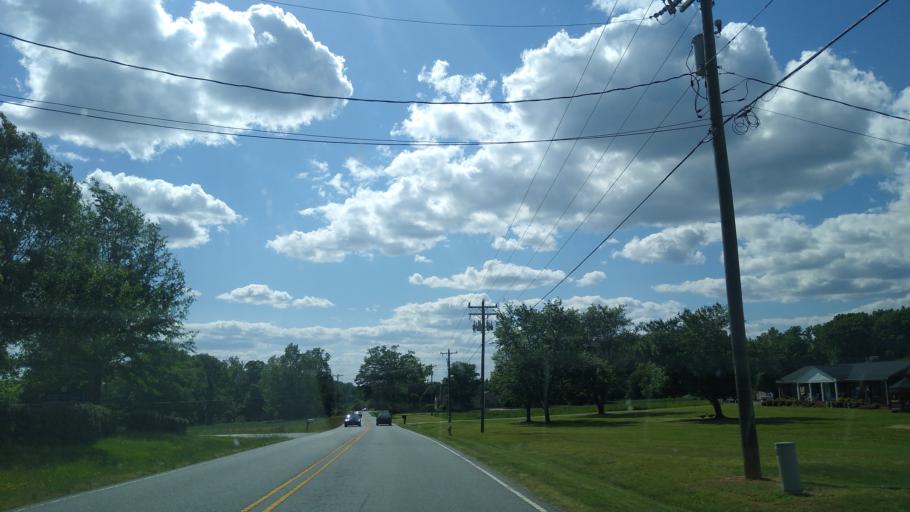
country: US
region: North Carolina
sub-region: Forsyth County
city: Kernersville
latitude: 36.1014
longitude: -80.0922
